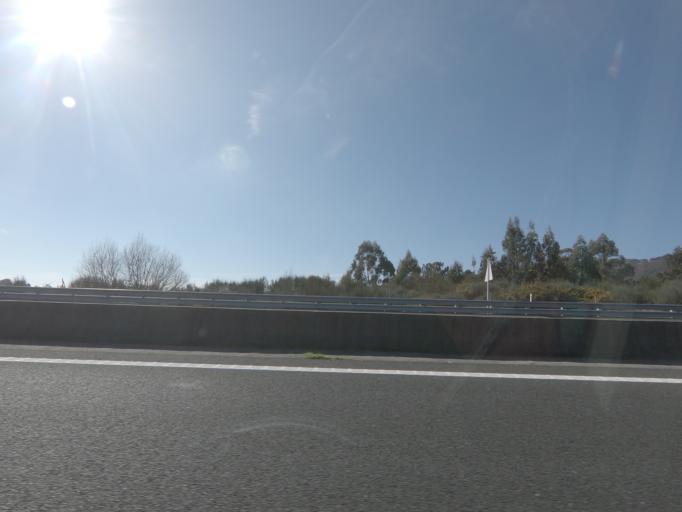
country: ES
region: Galicia
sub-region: Provincia de Ourense
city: Pinor
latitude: 42.4963
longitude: -8.0278
